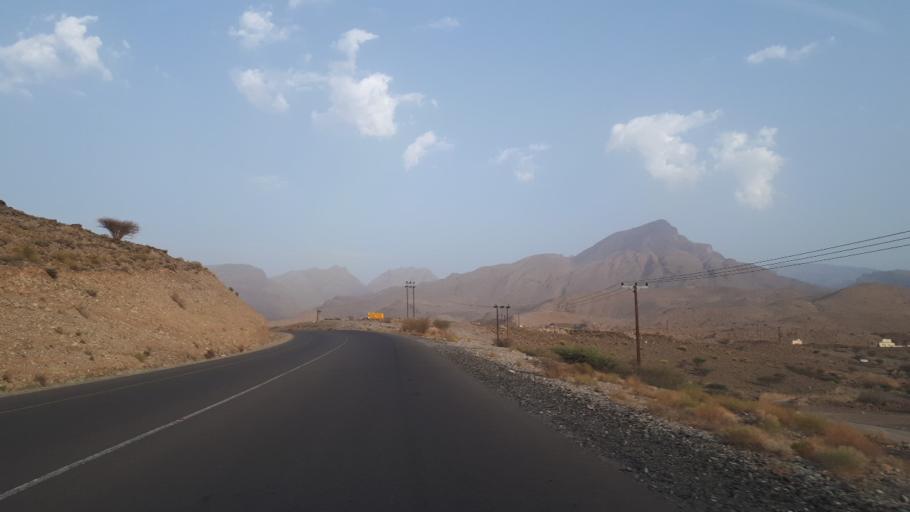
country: OM
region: Al Batinah
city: Rustaq
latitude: 23.3886
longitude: 57.2227
